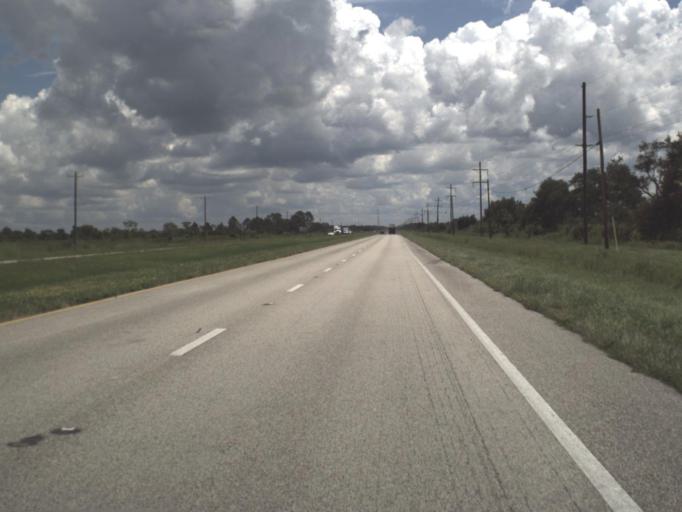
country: US
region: Florida
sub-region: Polk County
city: Babson Park
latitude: 27.8432
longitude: -81.3579
